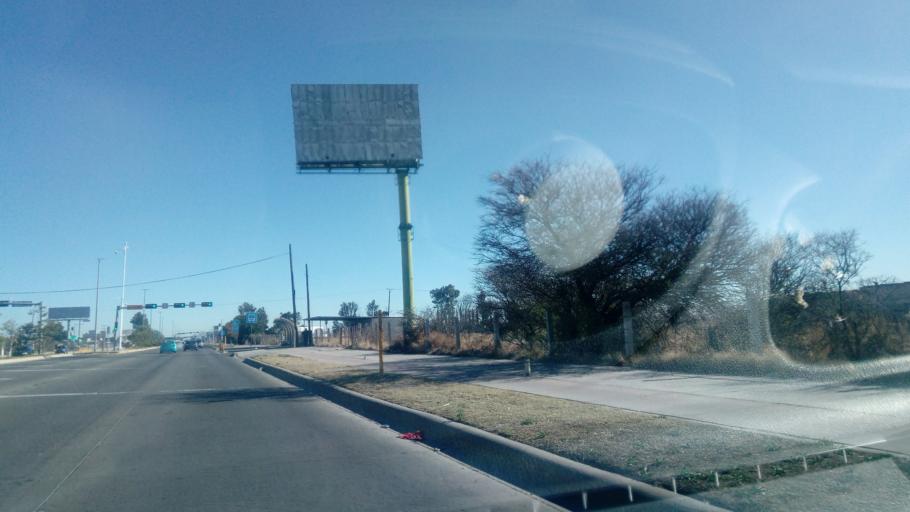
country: MX
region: Durango
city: Victoria de Durango
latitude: 24.0703
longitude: -104.5976
